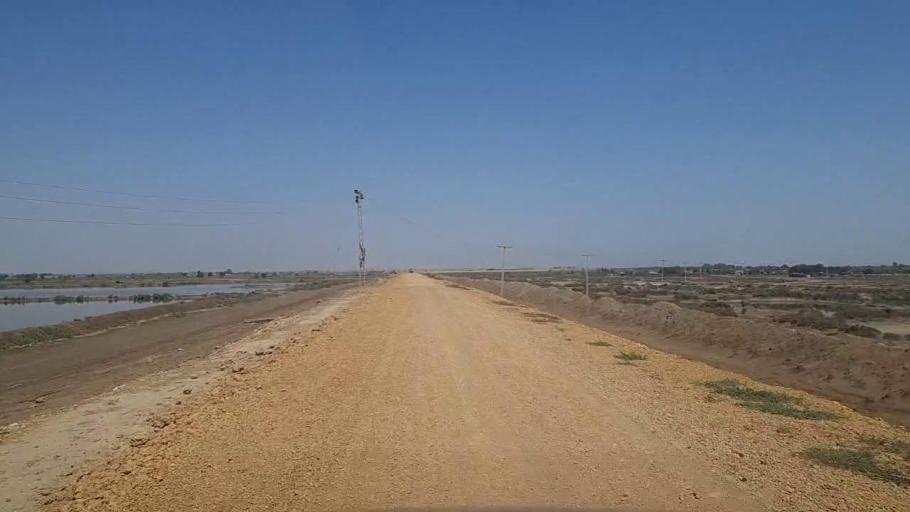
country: PK
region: Sindh
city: Thatta
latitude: 24.7872
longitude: 67.9967
